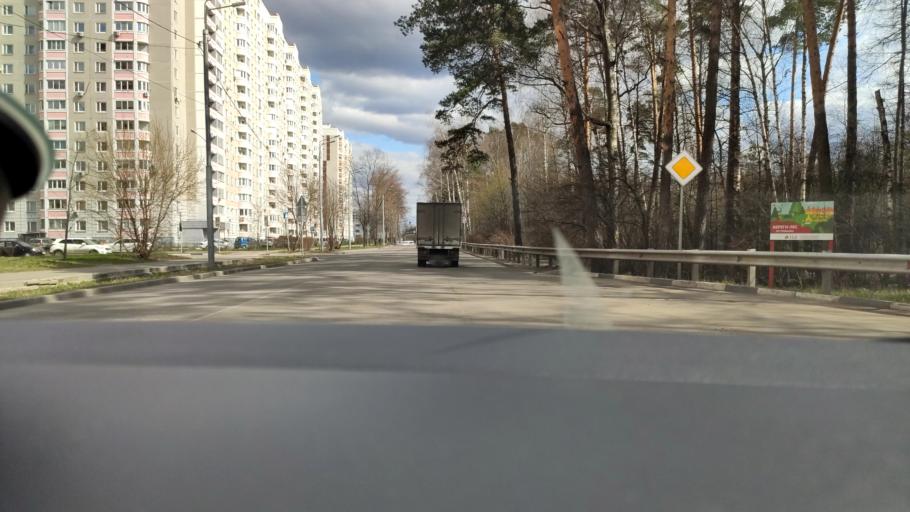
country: RU
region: Moskovskaya
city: Balashikha
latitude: 55.8211
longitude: 37.9438
